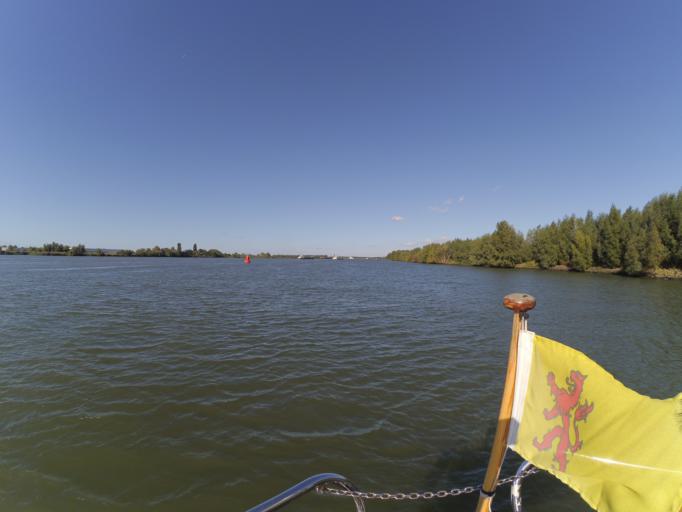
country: NL
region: South Holland
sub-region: Gemeente Binnenmaas
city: Heinenoord
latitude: 51.8336
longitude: 4.4487
